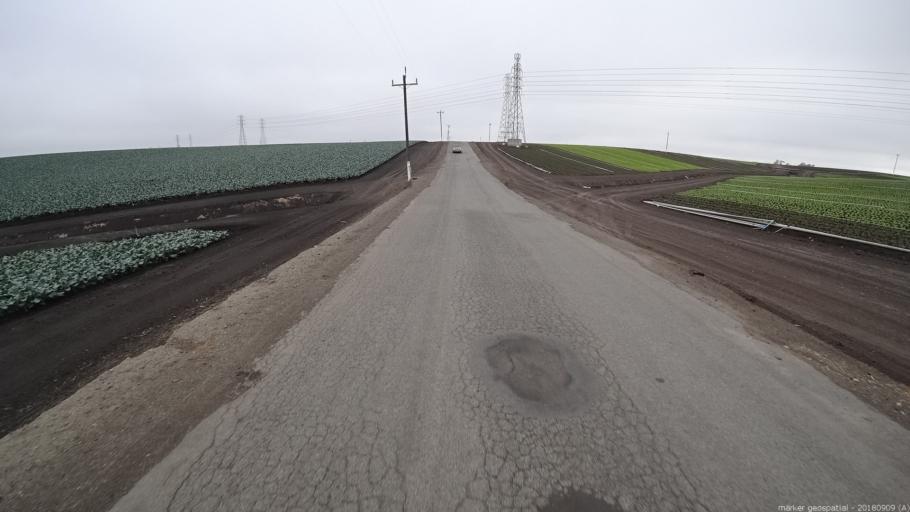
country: US
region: California
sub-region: Monterey County
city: Boronda
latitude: 36.7119
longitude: -121.6994
